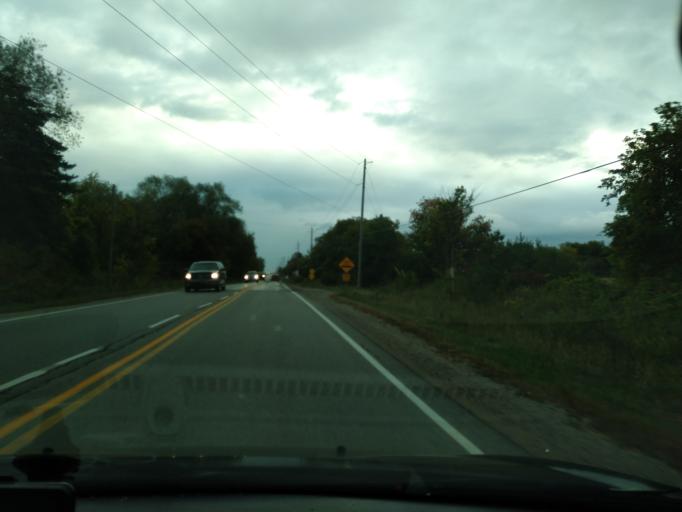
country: CA
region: Ontario
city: Innisfil
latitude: 44.2966
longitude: -79.5710
